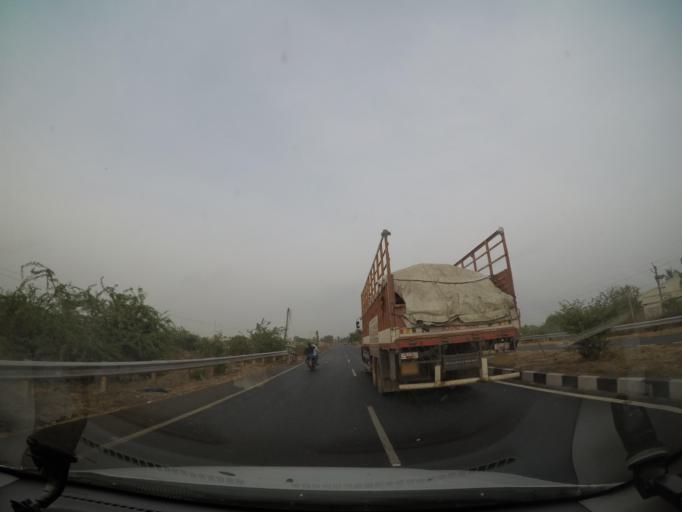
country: IN
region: Andhra Pradesh
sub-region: Krishna
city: Gannavaram
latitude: 16.6011
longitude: 80.8976
